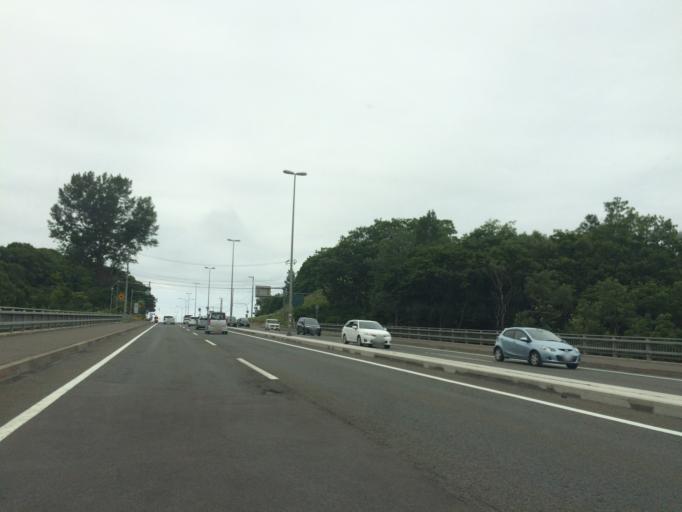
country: JP
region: Hokkaido
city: Otaru
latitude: 43.1590
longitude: 141.1107
